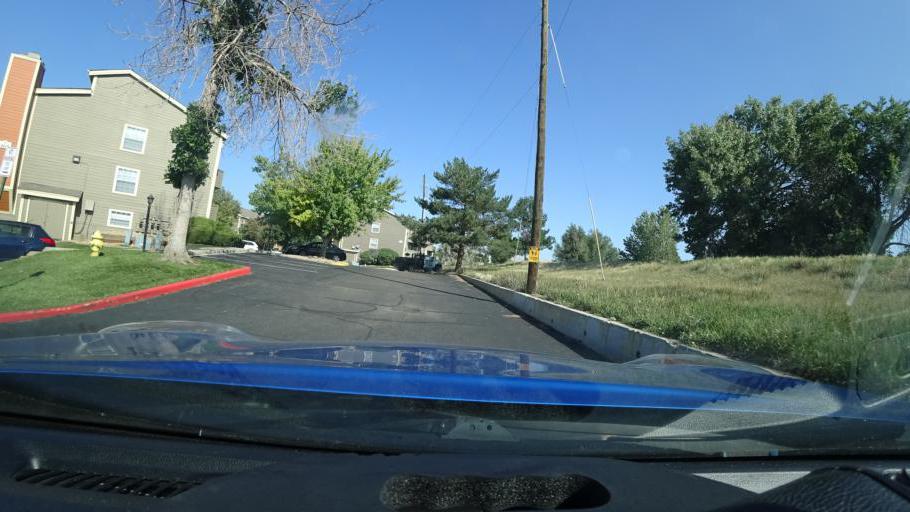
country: US
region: Colorado
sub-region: Adams County
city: Aurora
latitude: 39.7197
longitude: -104.8074
